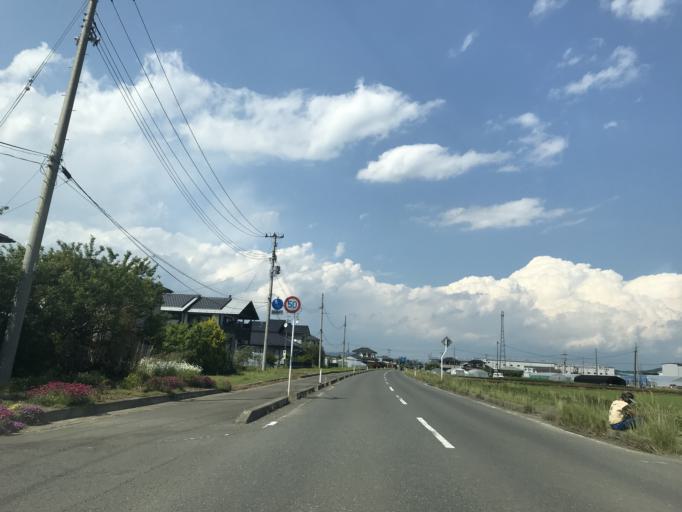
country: JP
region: Miyagi
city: Wakuya
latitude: 38.4670
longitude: 141.1298
